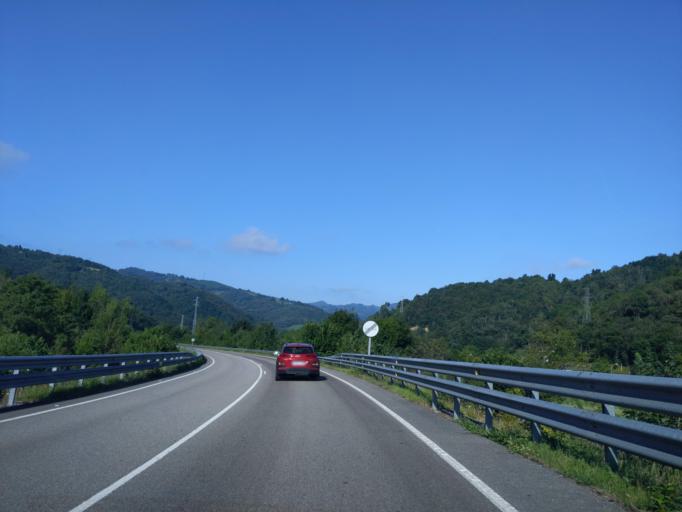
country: ES
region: Asturias
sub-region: Province of Asturias
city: Pola de Laviana
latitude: 43.2353
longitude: -5.5082
